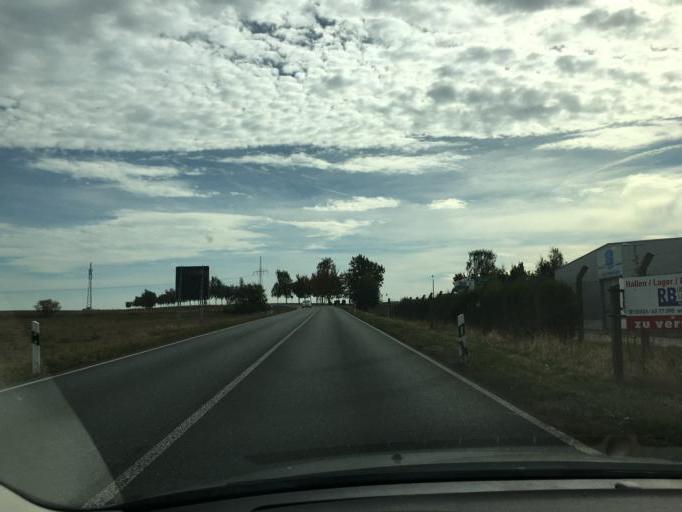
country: DE
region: Saxony
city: Stauchitz
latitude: 51.2636
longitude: 13.2617
